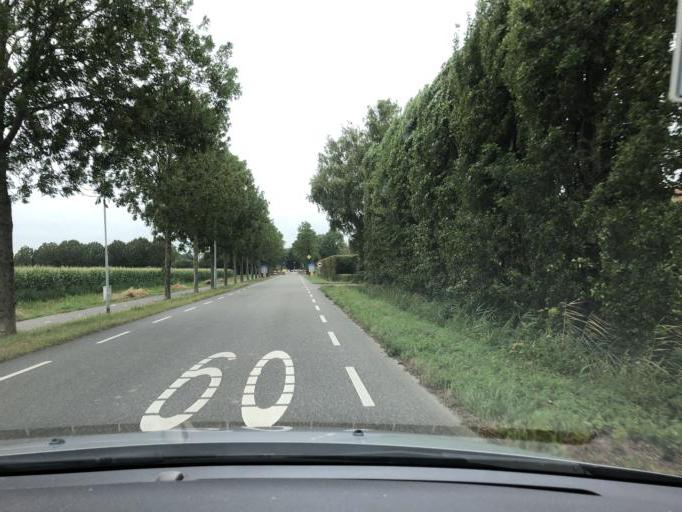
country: NL
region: North Brabant
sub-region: Gemeente Woensdrecht
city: Woensdrecht
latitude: 51.4141
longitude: 4.1893
